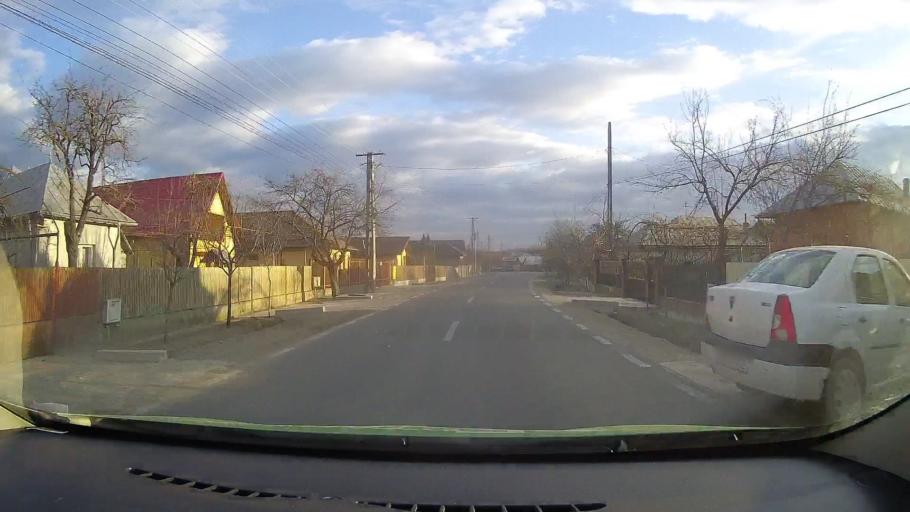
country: RO
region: Dambovita
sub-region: Comuna I. L. Caragiale
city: Ghirdoveni
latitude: 44.9512
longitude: 25.6583
